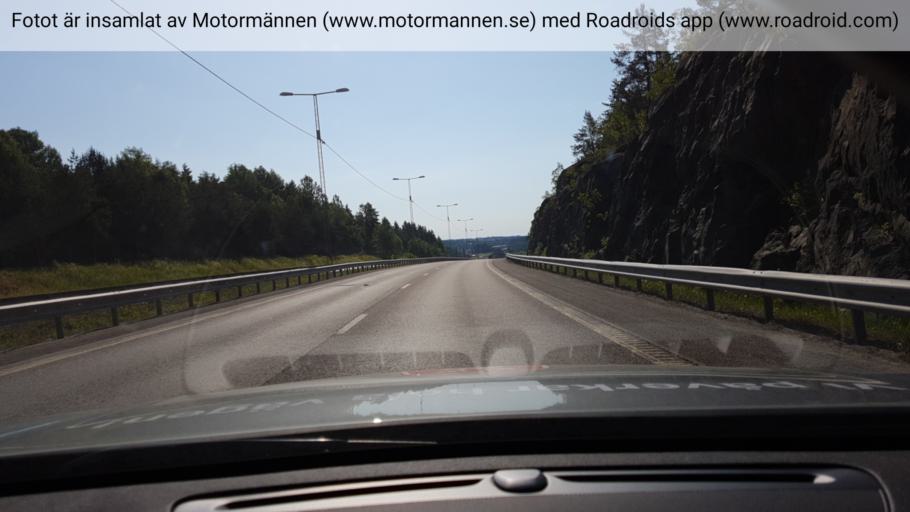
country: SE
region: Stockholm
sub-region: Osterakers Kommun
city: Akersberga
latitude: 59.4950
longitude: 18.2310
